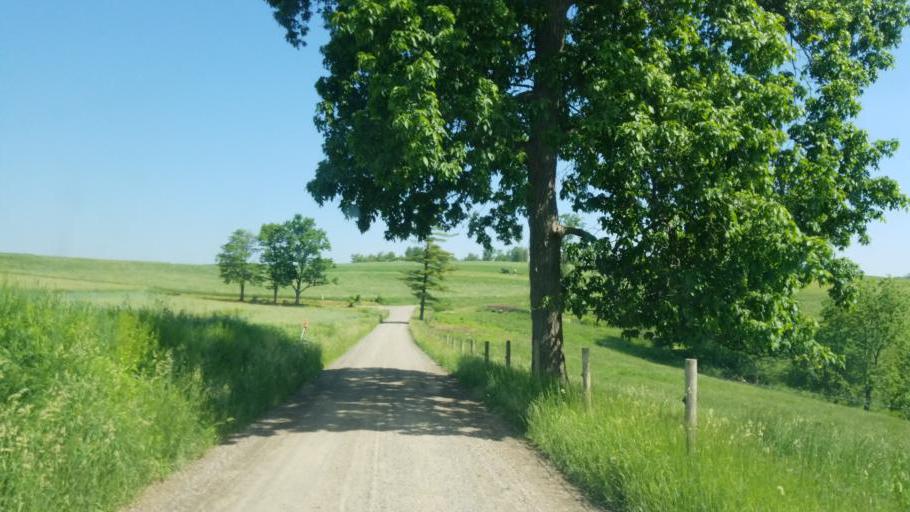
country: US
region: Ohio
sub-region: Holmes County
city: Millersburg
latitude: 40.4721
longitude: -81.7975
